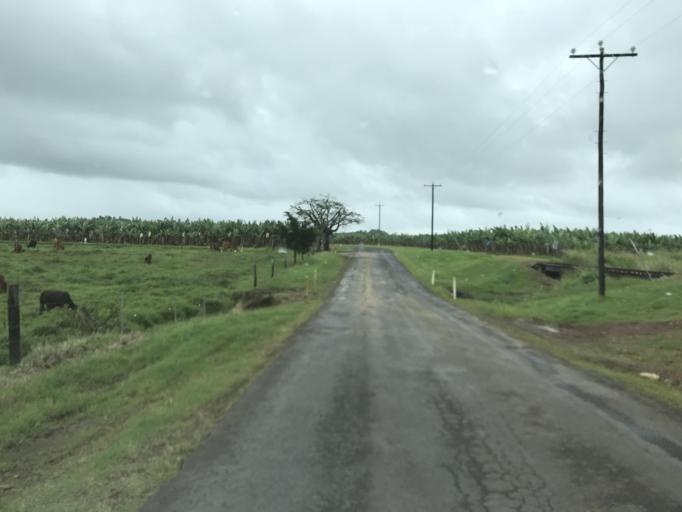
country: AU
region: Queensland
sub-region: Cassowary Coast
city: Innisfail
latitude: -17.5120
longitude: 145.9789
